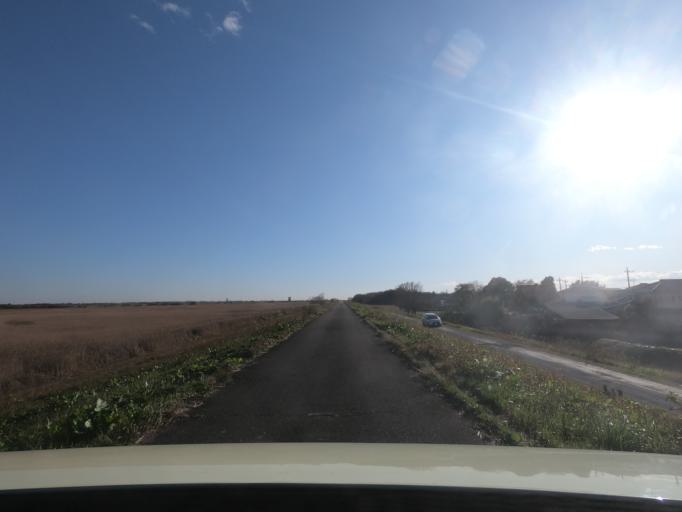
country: JP
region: Tochigi
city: Fujioka
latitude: 36.2707
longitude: 139.6801
